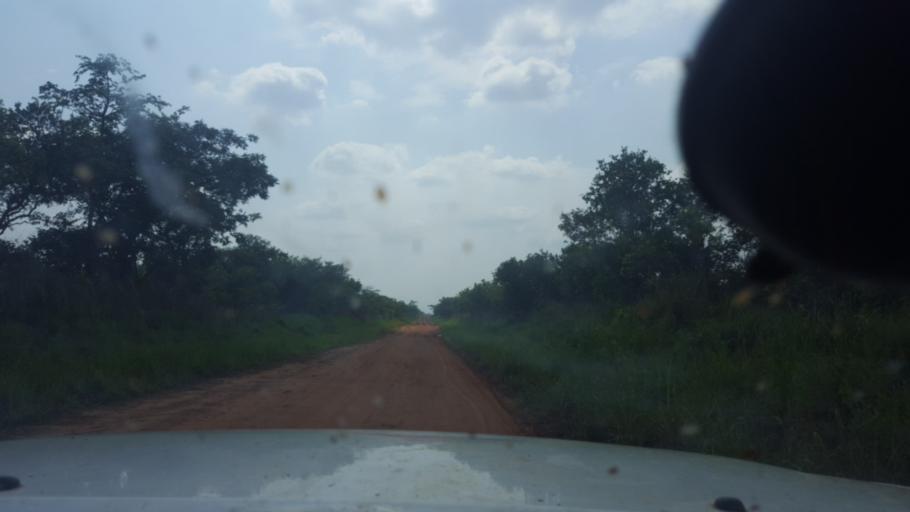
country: CD
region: Bandundu
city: Bandundu
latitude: -3.7620
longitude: 17.1460
